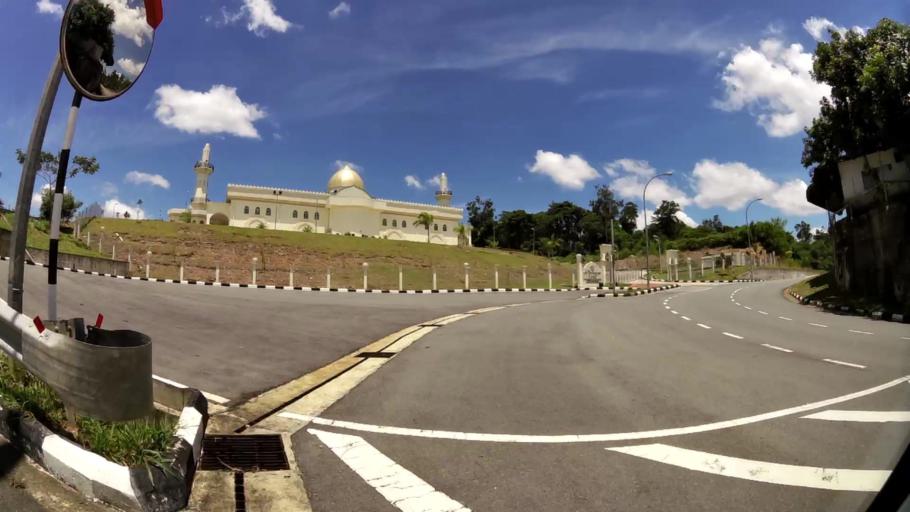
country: BN
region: Brunei and Muara
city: Bandar Seri Begawan
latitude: 4.9358
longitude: 114.9664
